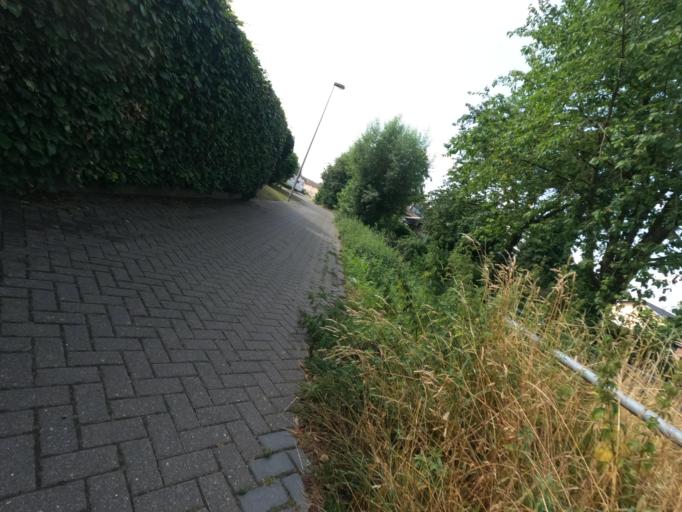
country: DE
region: North Rhine-Westphalia
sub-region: Regierungsbezirk Koln
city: Heinsberg
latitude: 51.0724
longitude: 6.1006
